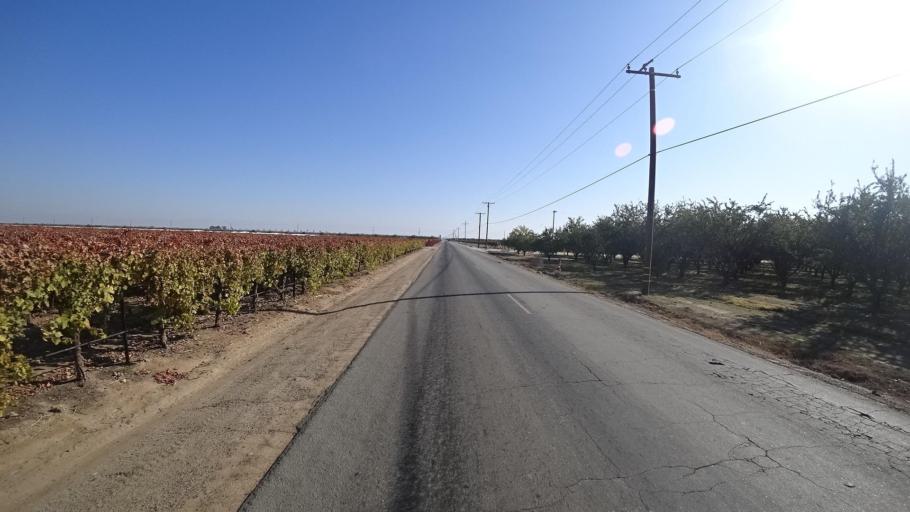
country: US
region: California
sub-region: Kern County
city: McFarland
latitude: 35.7179
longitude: -119.2103
